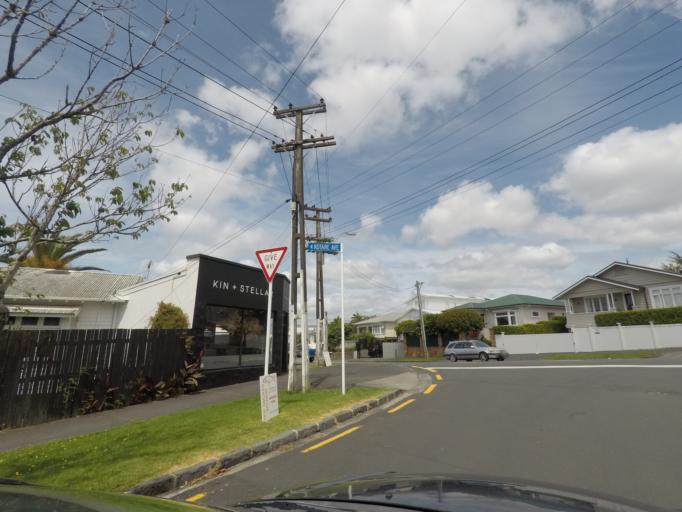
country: NZ
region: Auckland
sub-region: Auckland
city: Auckland
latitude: -36.8520
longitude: 174.7202
